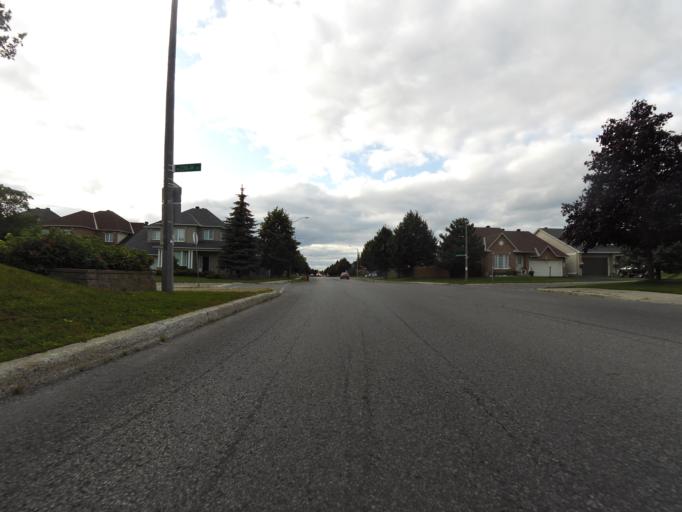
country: CA
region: Ontario
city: Bells Corners
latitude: 45.2775
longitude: -75.7269
